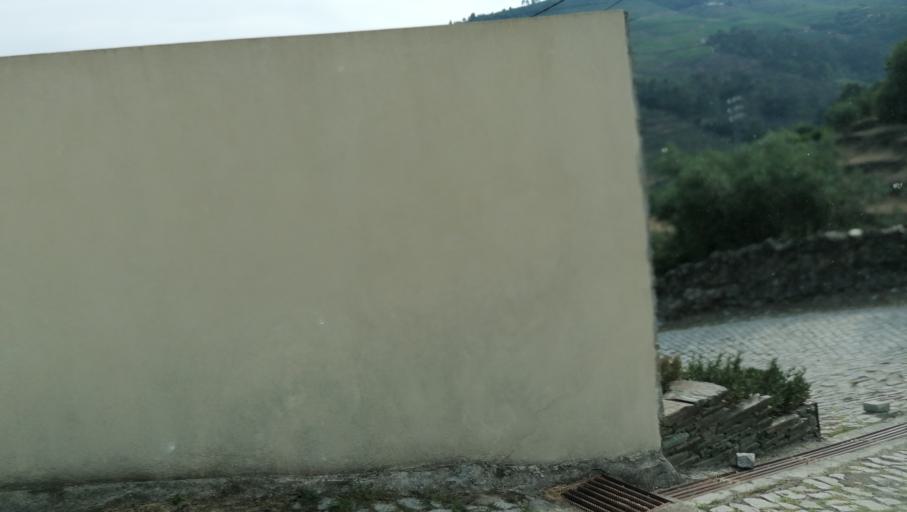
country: PT
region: Vila Real
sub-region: Sabrosa
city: Vilela
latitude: 41.1994
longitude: -7.5469
